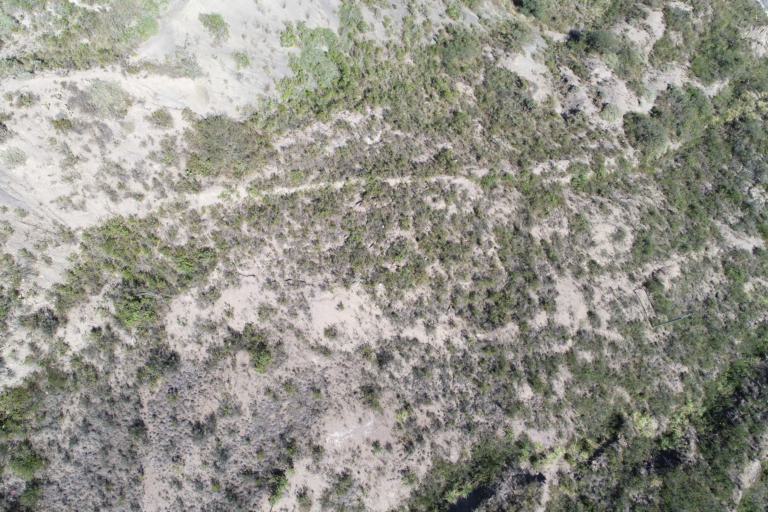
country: BO
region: La Paz
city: La Paz
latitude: -16.6212
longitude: -68.0387
